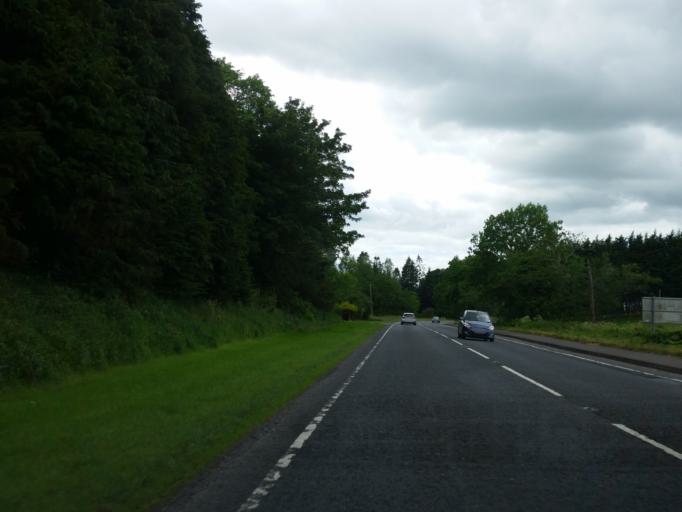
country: GB
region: Northern Ireland
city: Fivemiletown
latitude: 54.4205
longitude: -7.1480
